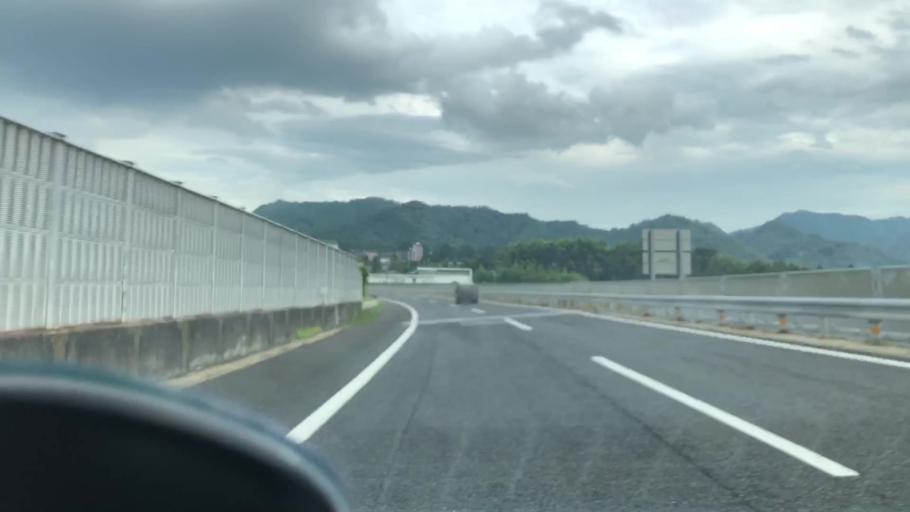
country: JP
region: Hyogo
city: Yamazakicho-nakabirose
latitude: 34.9646
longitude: 134.6793
